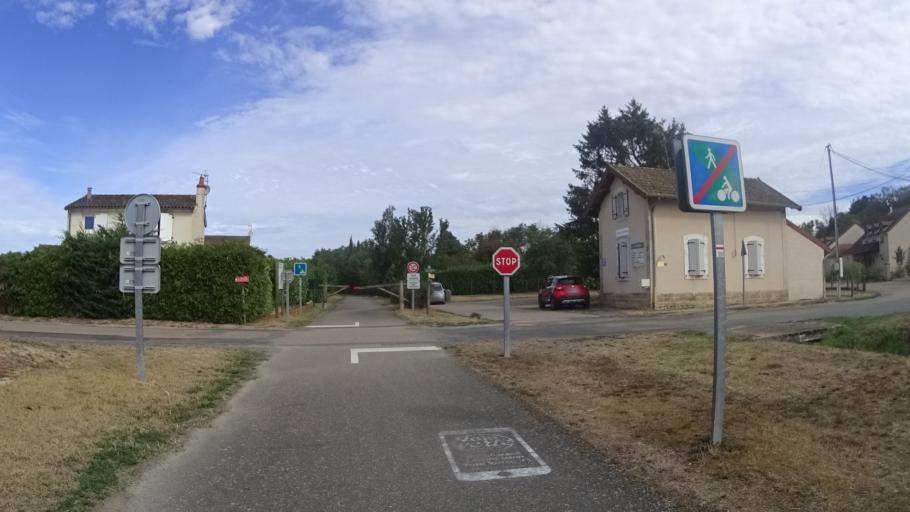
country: FR
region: Auvergne
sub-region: Departement de l'Allier
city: Diou
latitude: 46.5690
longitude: 3.7494
